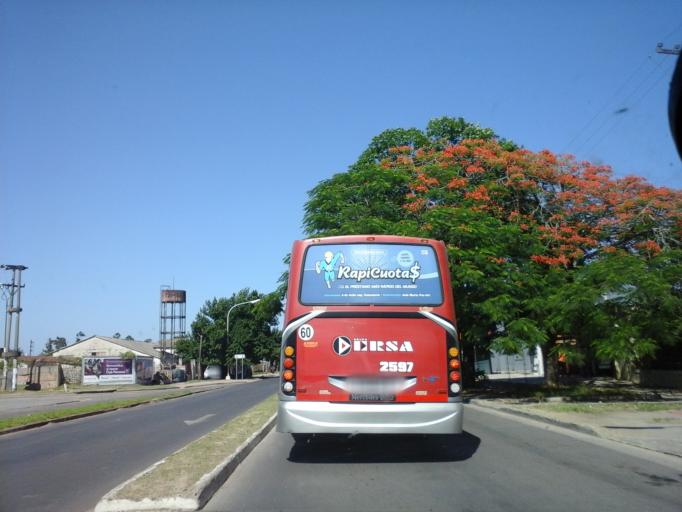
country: AR
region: Corrientes
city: Corrientes
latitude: -27.4667
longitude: -58.7902
